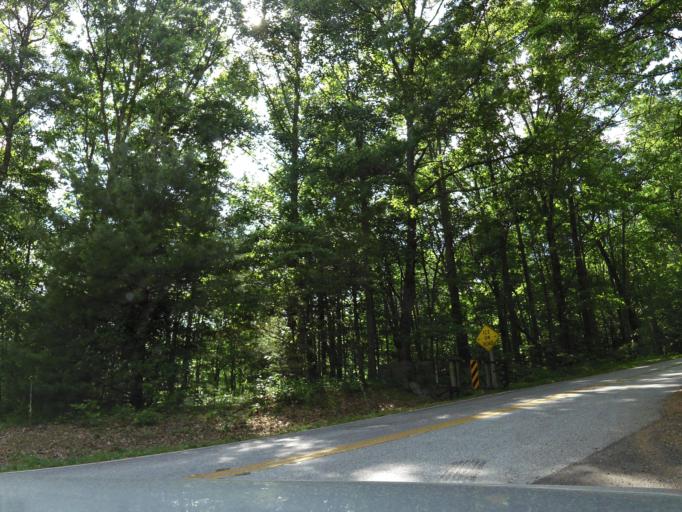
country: US
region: Georgia
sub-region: Towns County
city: Hiawassee
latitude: 34.8483
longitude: -83.7988
